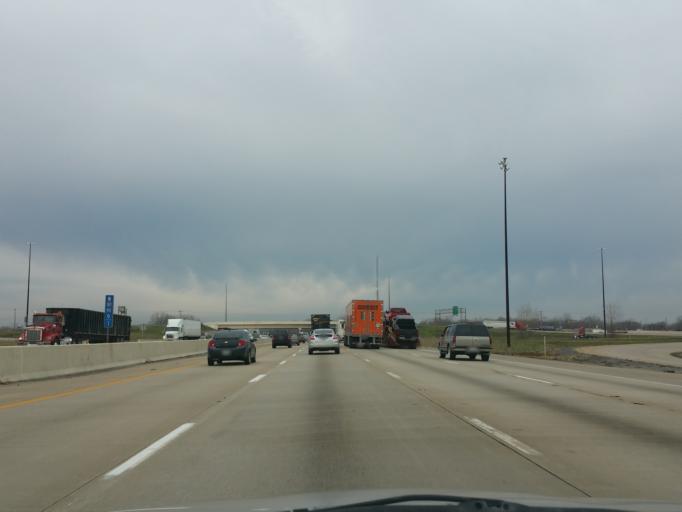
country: US
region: Indiana
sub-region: Lake County
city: Gary
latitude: 41.5684
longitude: -87.3514
